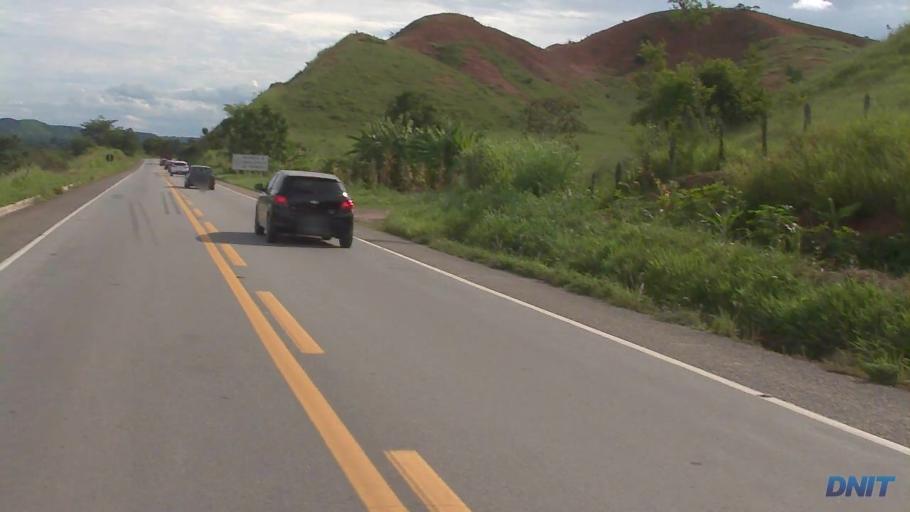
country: BR
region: Minas Gerais
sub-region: Belo Oriente
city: Belo Oriente
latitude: -19.1780
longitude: -42.2573
